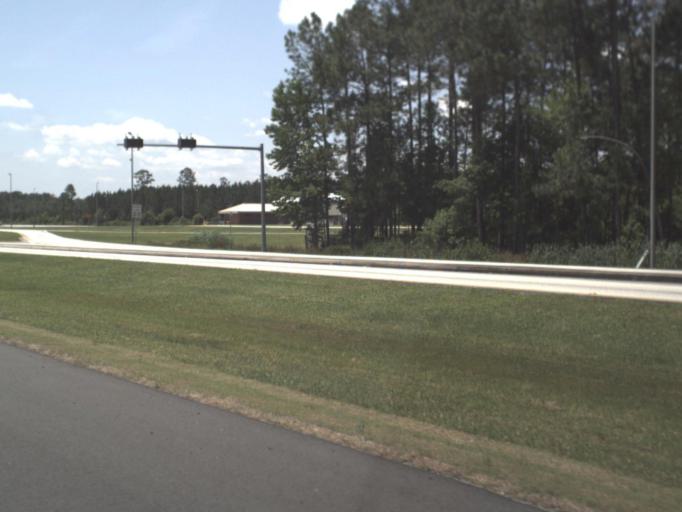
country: US
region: Florida
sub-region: Nassau County
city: Yulee
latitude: 30.6718
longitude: -81.6686
